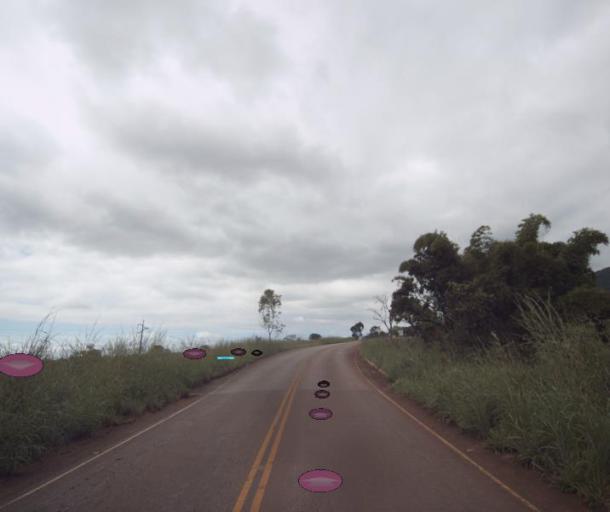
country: BR
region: Goias
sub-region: Barro Alto
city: Barro Alto
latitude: -14.9870
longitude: -48.9100
